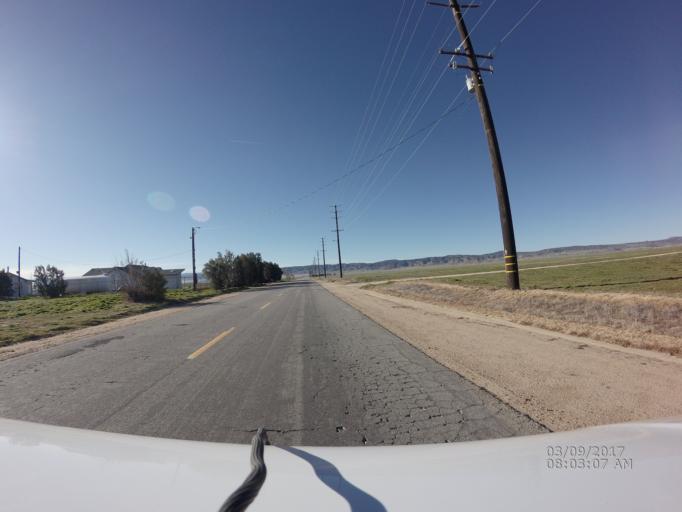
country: US
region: California
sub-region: Los Angeles County
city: Leona Valley
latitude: 34.7400
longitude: -118.3247
